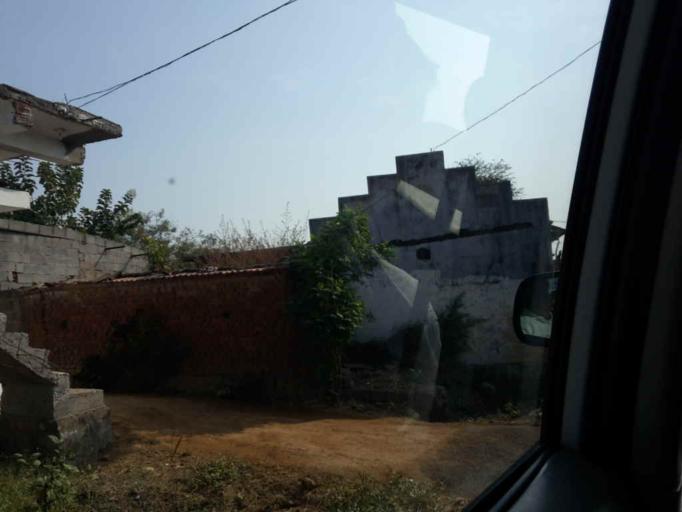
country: IN
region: Telangana
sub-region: Karimnagar
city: Vemalwada
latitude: 18.4012
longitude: 78.9861
